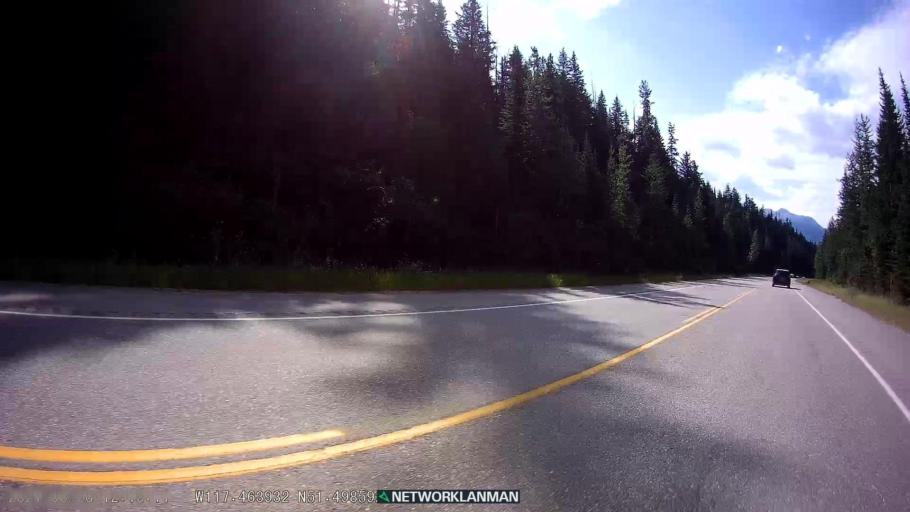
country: CA
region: British Columbia
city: Golden
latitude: 51.4983
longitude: -117.4625
